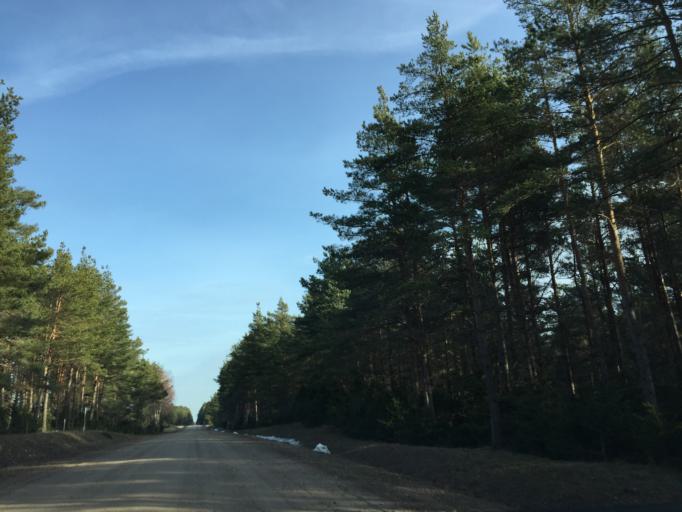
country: EE
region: Saare
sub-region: Kuressaare linn
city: Kuressaare
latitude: 58.2836
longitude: 21.9227
